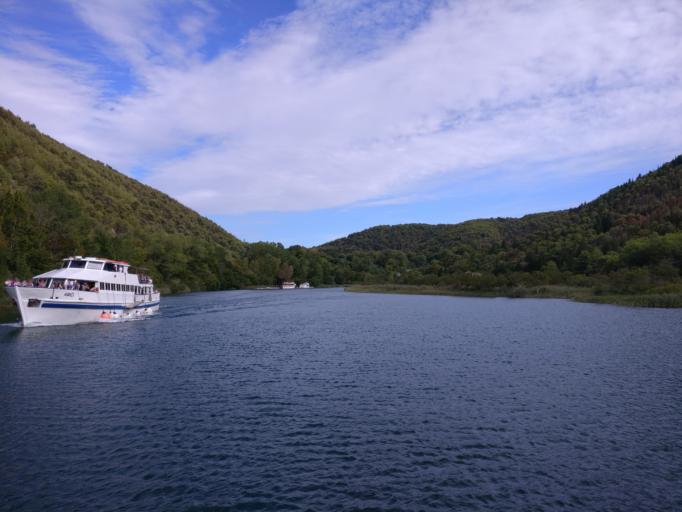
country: HR
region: Sibensko-Kniniska
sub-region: Grad Sibenik
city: Sibenik
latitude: 43.8094
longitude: 15.9576
